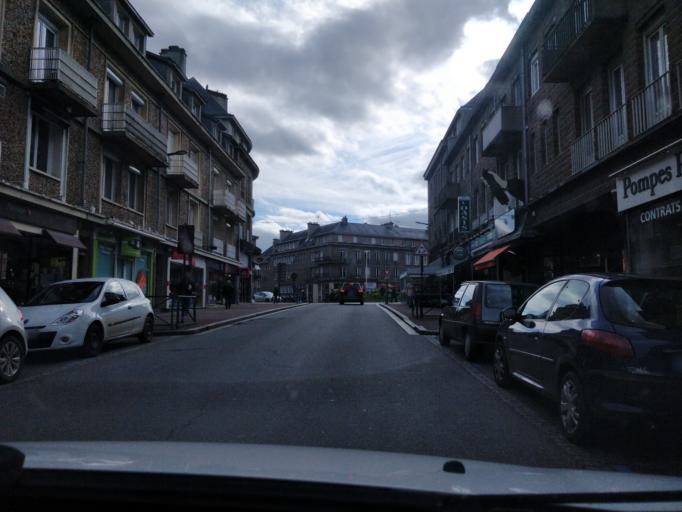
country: FR
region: Lower Normandy
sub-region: Departement du Calvados
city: Vire
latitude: 48.8392
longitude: -0.8889
